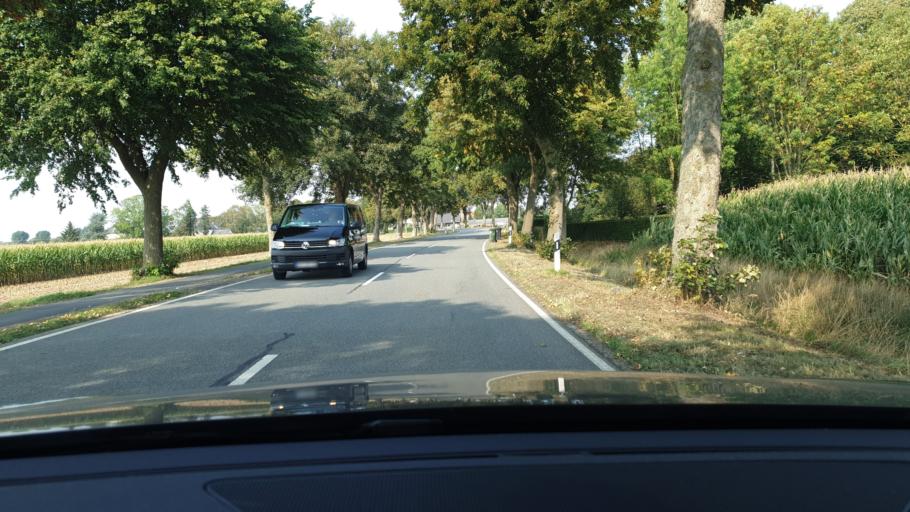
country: NL
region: Gelderland
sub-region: Gemeente Zevenaar
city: Zevenaar
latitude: 51.8534
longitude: 6.0725
